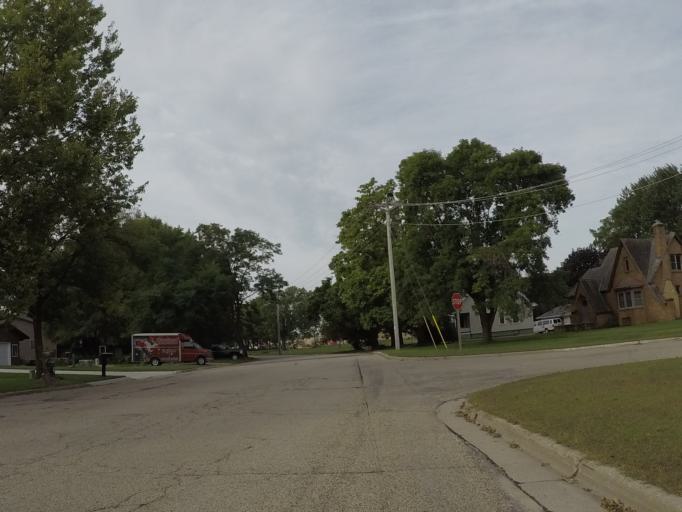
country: US
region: Wisconsin
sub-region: Sauk County
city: Sauk City
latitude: 43.2676
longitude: -89.7258
